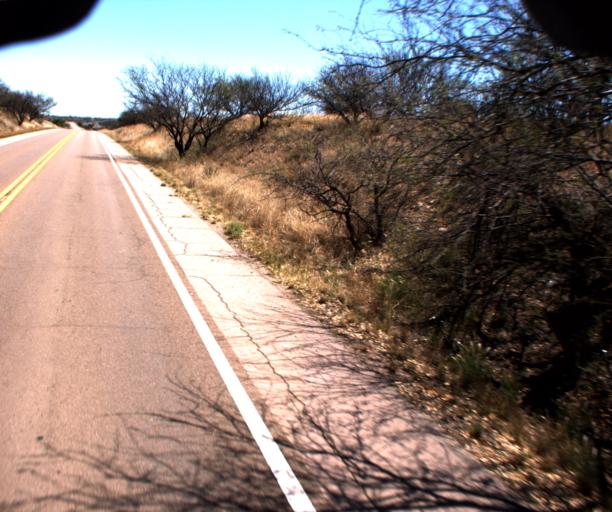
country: US
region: Arizona
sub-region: Pima County
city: Corona de Tucson
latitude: 31.6569
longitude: -110.7034
